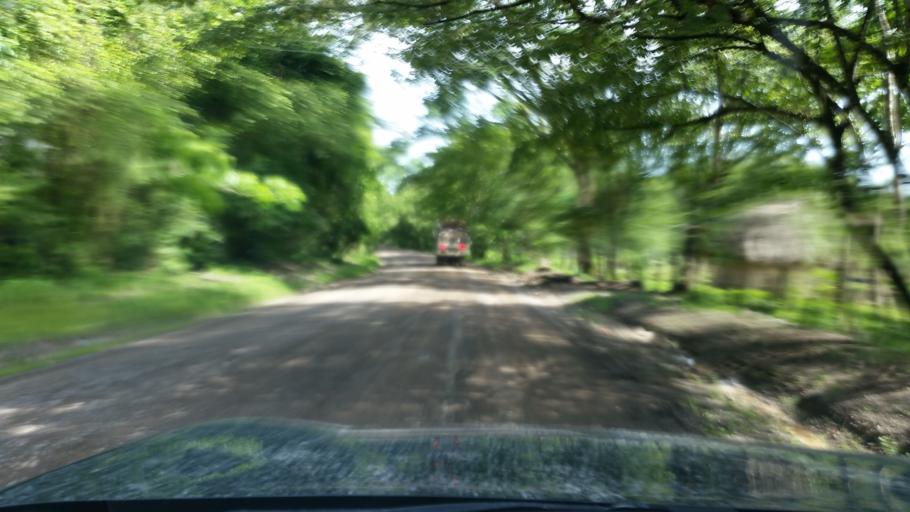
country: NI
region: Atlantico Norte (RAAN)
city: Siuna
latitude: 13.6805
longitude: -84.7903
